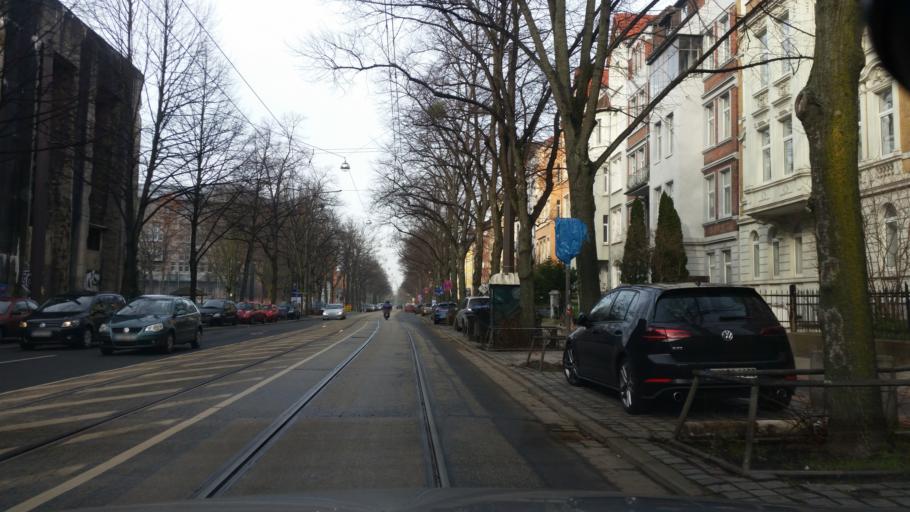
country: DE
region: Lower Saxony
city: Hannover
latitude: 52.3918
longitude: 9.7197
